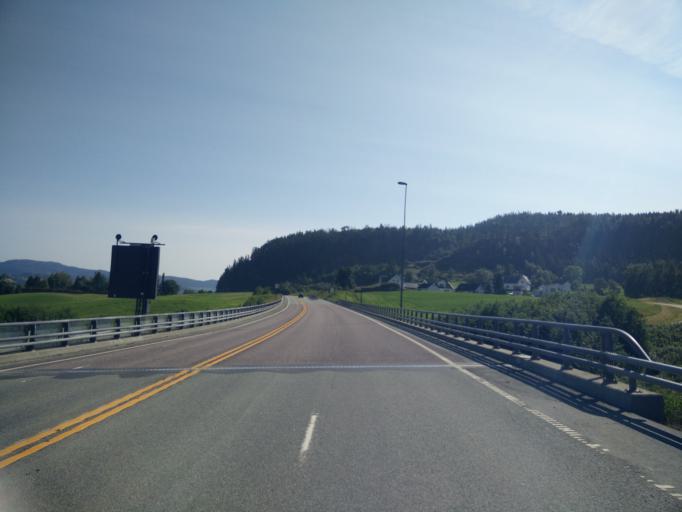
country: NO
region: Sor-Trondelag
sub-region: Skaun
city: Borsa
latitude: 63.3221
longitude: 10.0687
